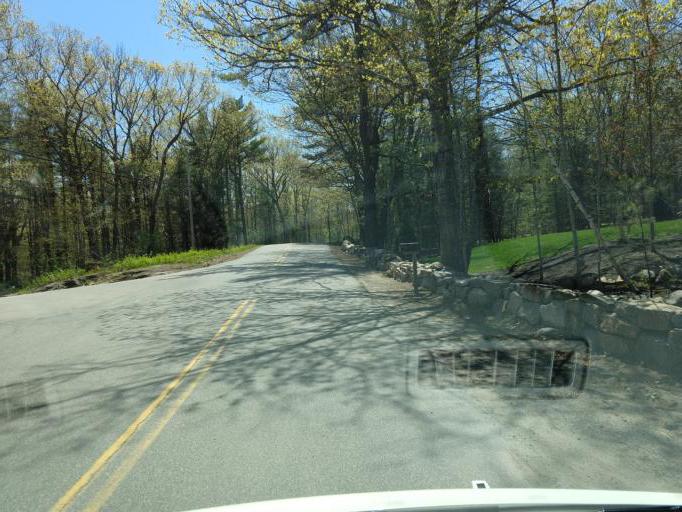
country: US
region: Maine
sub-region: York County
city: Cape Neddick
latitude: 43.2261
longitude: -70.6287
